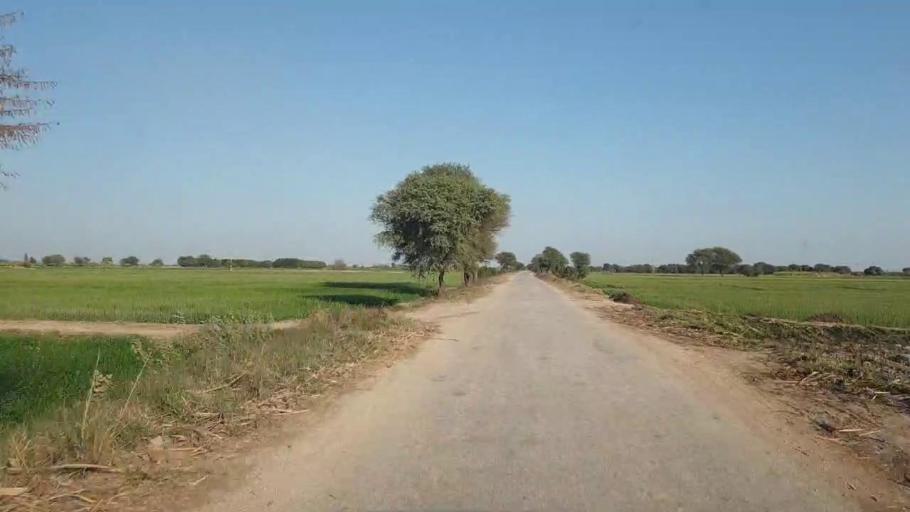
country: PK
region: Sindh
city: Tando Allahyar
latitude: 25.3816
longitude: 68.6777
